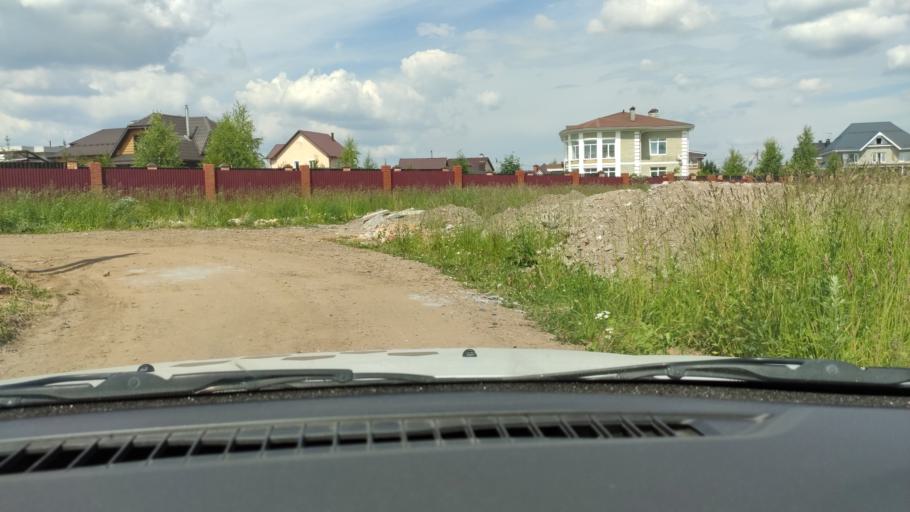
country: RU
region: Perm
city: Perm
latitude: 58.0369
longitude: 56.3750
